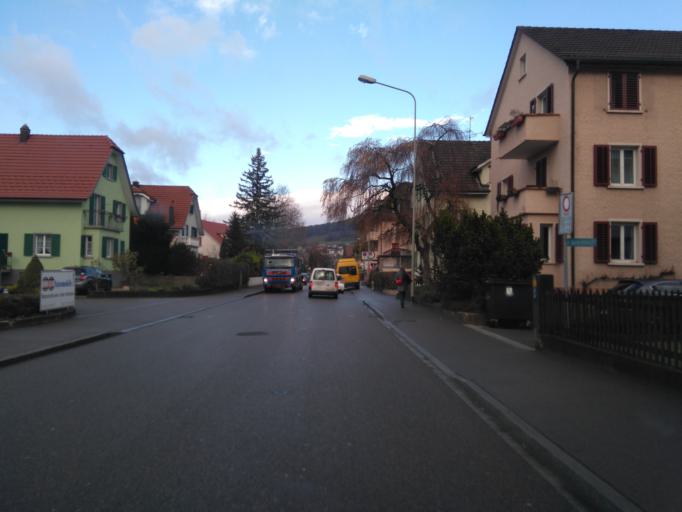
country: CH
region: Zurich
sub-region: Bezirk Dietikon
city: Schlieren / Engstingerquartier
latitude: 47.4046
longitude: 8.4478
